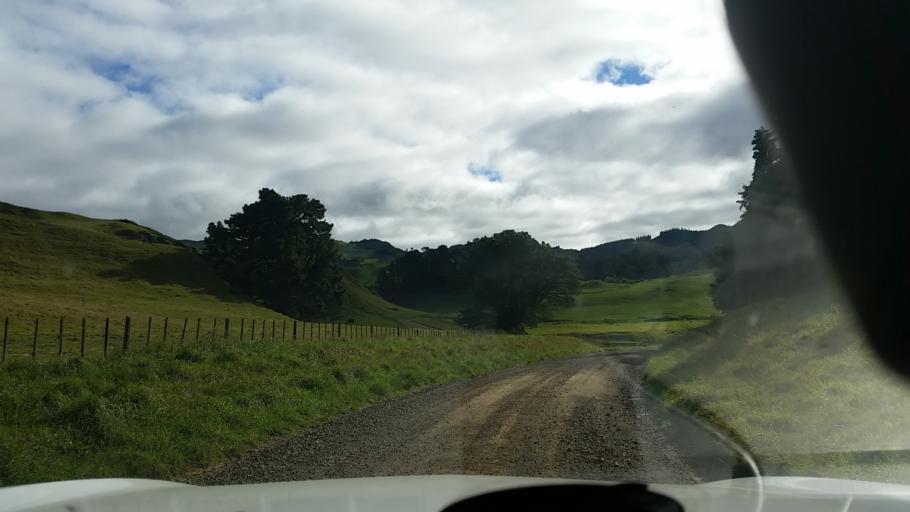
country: NZ
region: Hawke's Bay
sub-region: Napier City
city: Napier
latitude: -39.1007
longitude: 176.8747
